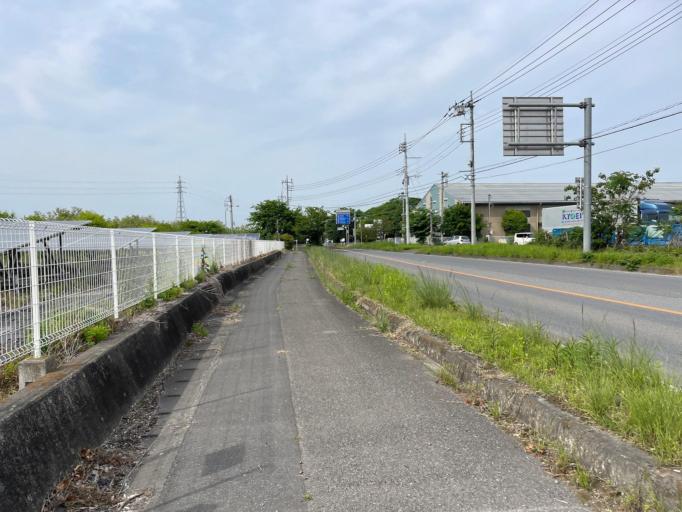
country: JP
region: Tochigi
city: Mibu
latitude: 36.4068
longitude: 139.8044
